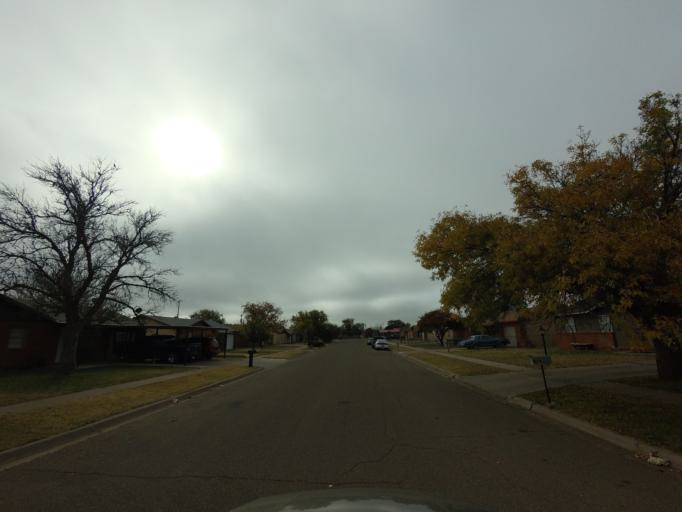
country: US
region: New Mexico
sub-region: Curry County
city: Clovis
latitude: 34.4294
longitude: -103.2283
